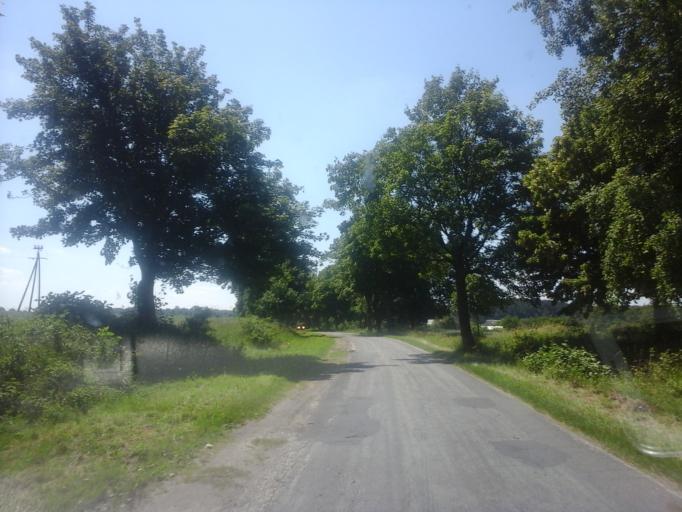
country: PL
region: West Pomeranian Voivodeship
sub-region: Powiat bialogardzki
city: Bialogard
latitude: 54.0769
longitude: 16.0458
